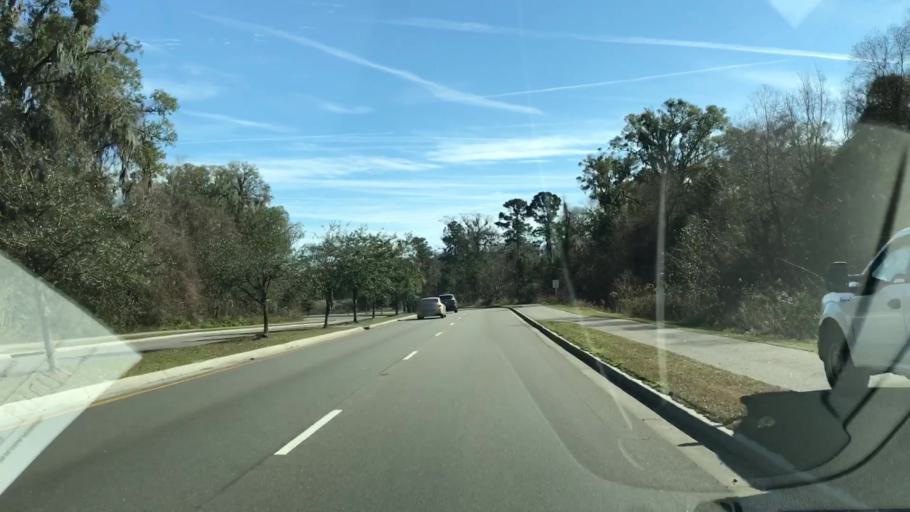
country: US
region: South Carolina
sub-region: Beaufort County
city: Bluffton
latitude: 32.2633
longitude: -80.8773
